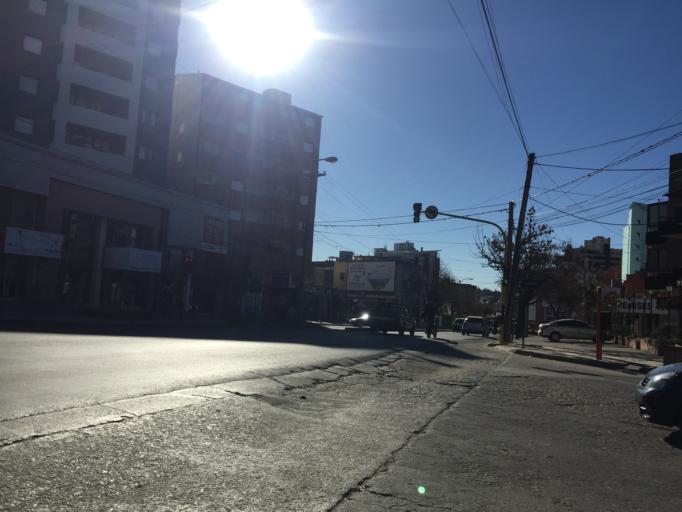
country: AR
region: Cordoba
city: Villa Carlos Paz
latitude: -31.4238
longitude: -64.4953
